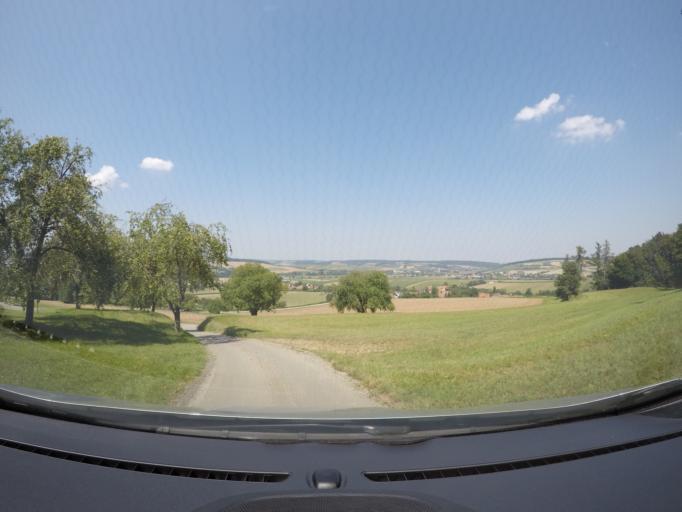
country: AT
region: Lower Austria
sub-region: Politischer Bezirk Sankt Polten
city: Maria-Anzbach
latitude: 48.2153
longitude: 15.9321
